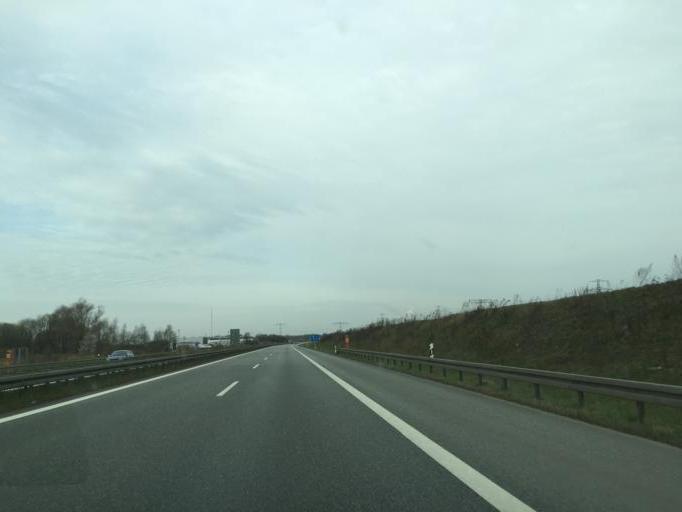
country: DE
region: Mecklenburg-Vorpommern
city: Dierkow-Neu
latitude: 54.1117
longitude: 12.1796
